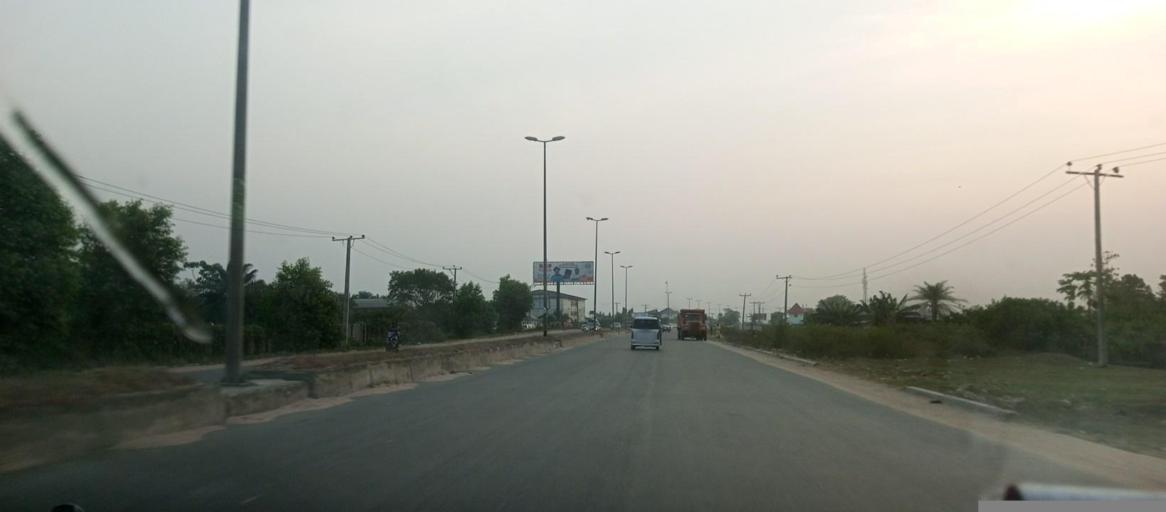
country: NG
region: Rivers
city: Emuoha
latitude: 4.9368
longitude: 7.0063
